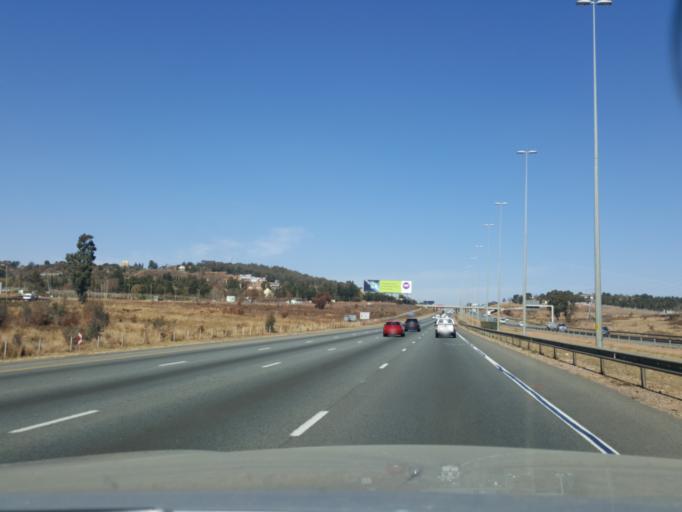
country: ZA
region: Gauteng
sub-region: City of Tshwane Metropolitan Municipality
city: Centurion
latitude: -25.8800
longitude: 28.2548
